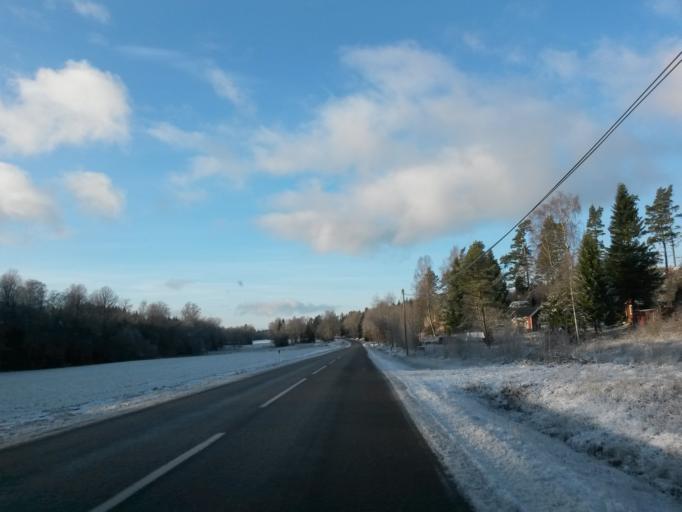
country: SE
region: Vaestra Goetaland
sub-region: Vargarda Kommun
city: Jonstorp
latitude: 58.0616
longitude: 12.7029
